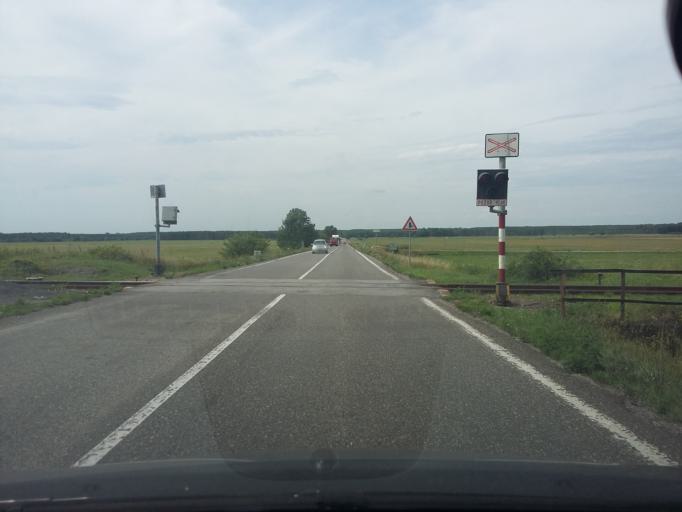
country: SK
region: Bratislavsky
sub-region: Okres Malacky
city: Malacky
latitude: 48.3792
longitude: 17.1215
